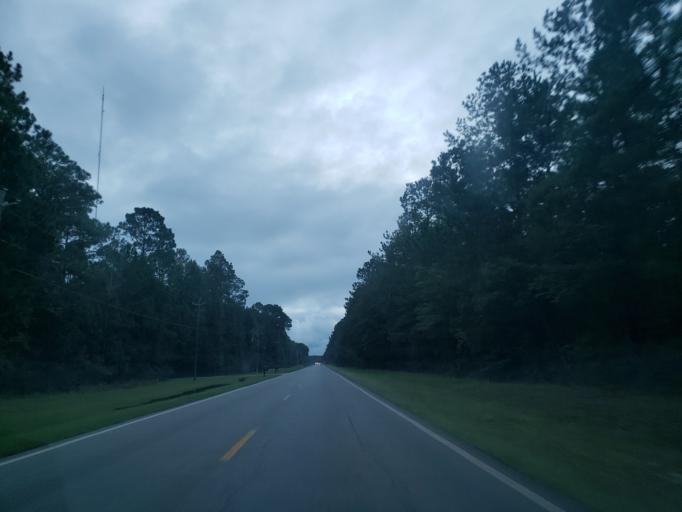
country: US
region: Georgia
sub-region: Chatham County
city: Bloomingdale
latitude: 32.0586
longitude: -81.3078
